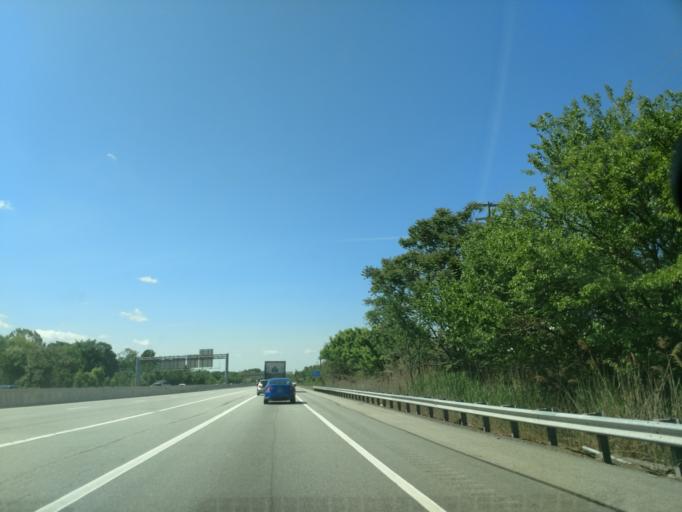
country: US
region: Pennsylvania
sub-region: Montgomery County
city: King of Prussia
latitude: 40.0819
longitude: -75.4083
